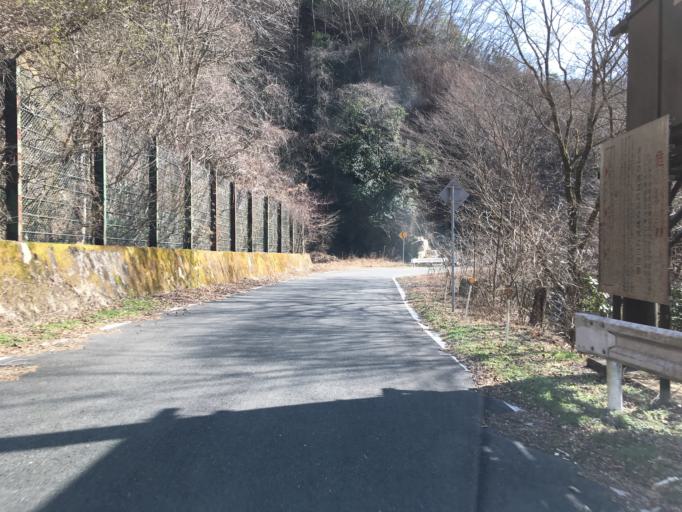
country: JP
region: Ibaraki
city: Kitaibaraki
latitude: 36.7883
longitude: 140.6636
